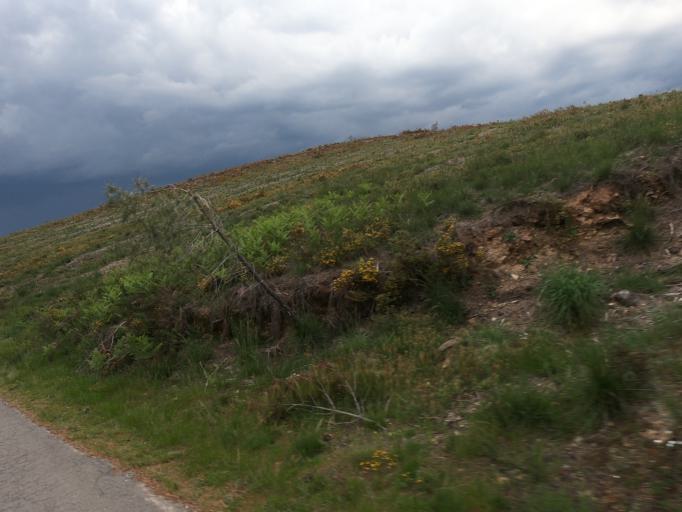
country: PT
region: Vila Real
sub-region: Sabrosa
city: Vilela
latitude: 41.2387
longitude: -7.6690
